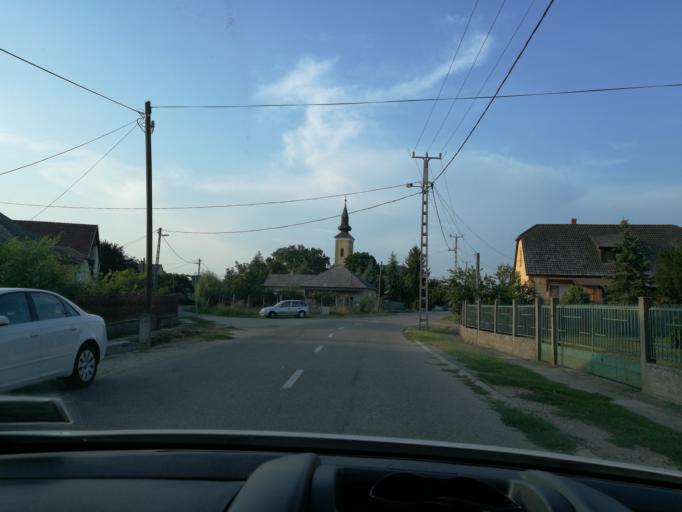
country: HU
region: Szabolcs-Szatmar-Bereg
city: Nyirpazony
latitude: 47.9508
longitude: 21.8048
